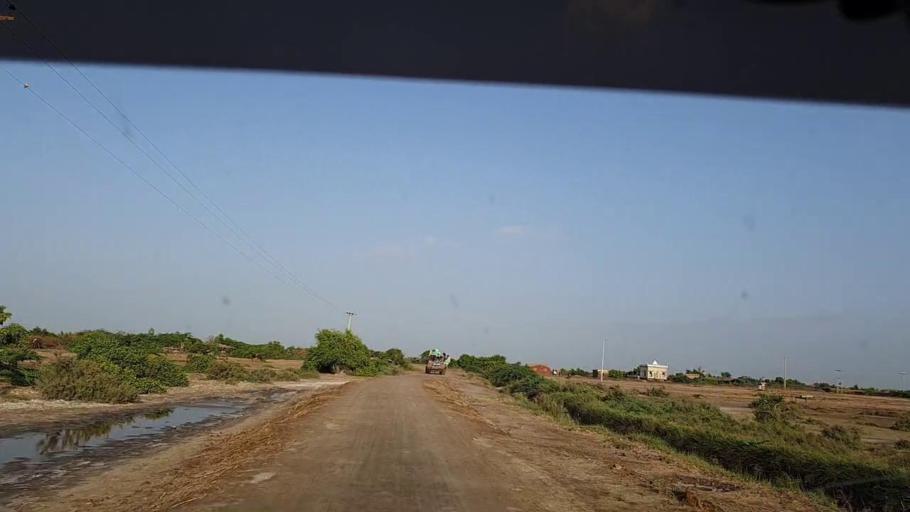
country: PK
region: Sindh
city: Badin
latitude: 24.5524
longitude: 68.8678
